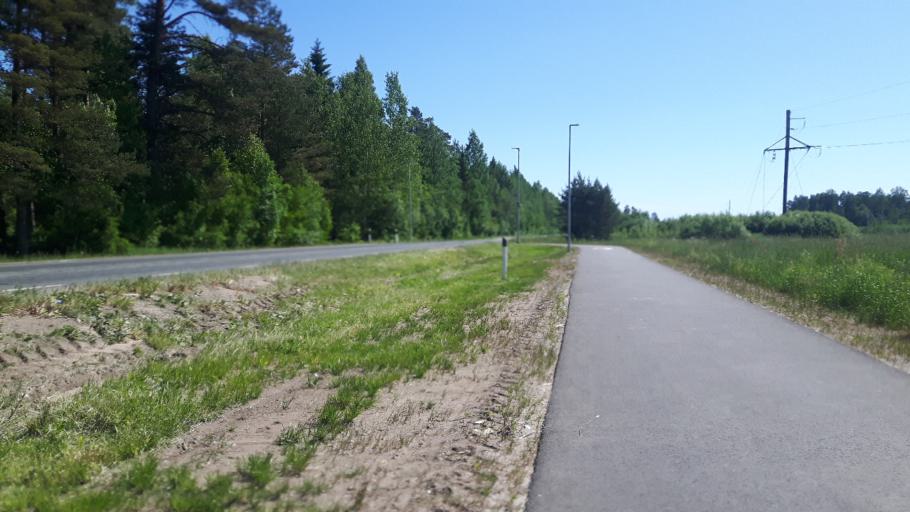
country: EE
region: Raplamaa
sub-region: Kohila vald
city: Kohila
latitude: 59.2102
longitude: 24.6835
